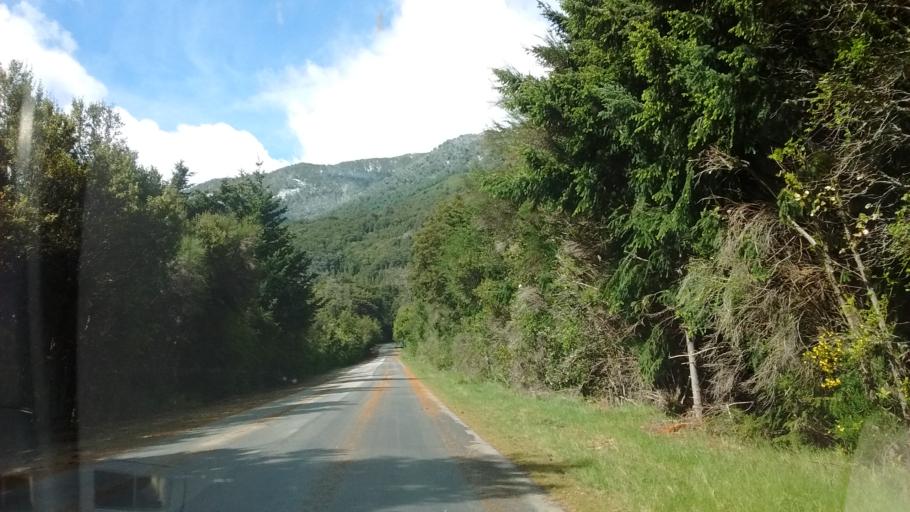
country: AR
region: Rio Negro
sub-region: Departamento de Bariloche
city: San Carlos de Bariloche
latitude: -41.0807
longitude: -71.5450
